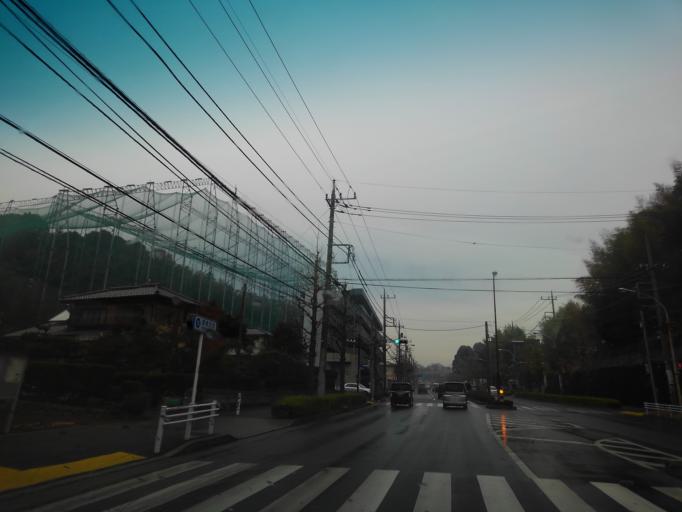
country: JP
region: Tokyo
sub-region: Machida-shi
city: Machida
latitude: 35.6049
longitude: 139.4447
